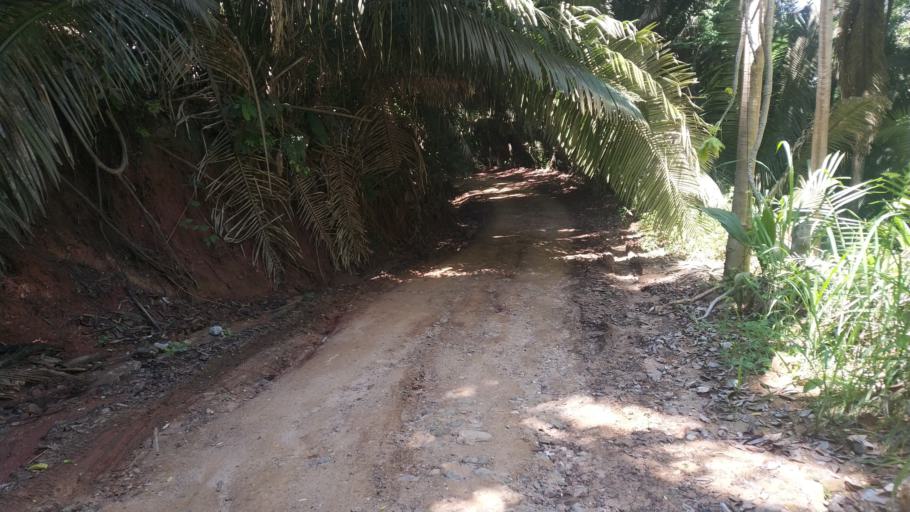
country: MX
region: Nayarit
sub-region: Bahia de Banderas
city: Lo de Marcos
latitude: 20.9286
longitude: -105.3977
